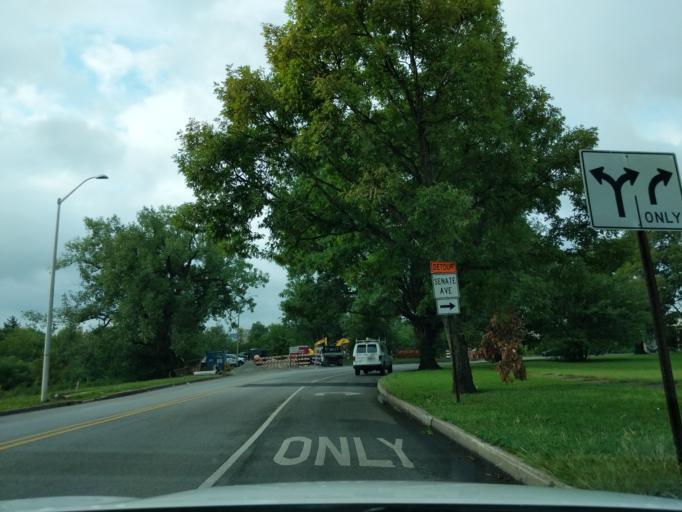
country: US
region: Indiana
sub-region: Marion County
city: Indianapolis
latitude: 39.7988
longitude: -86.1643
